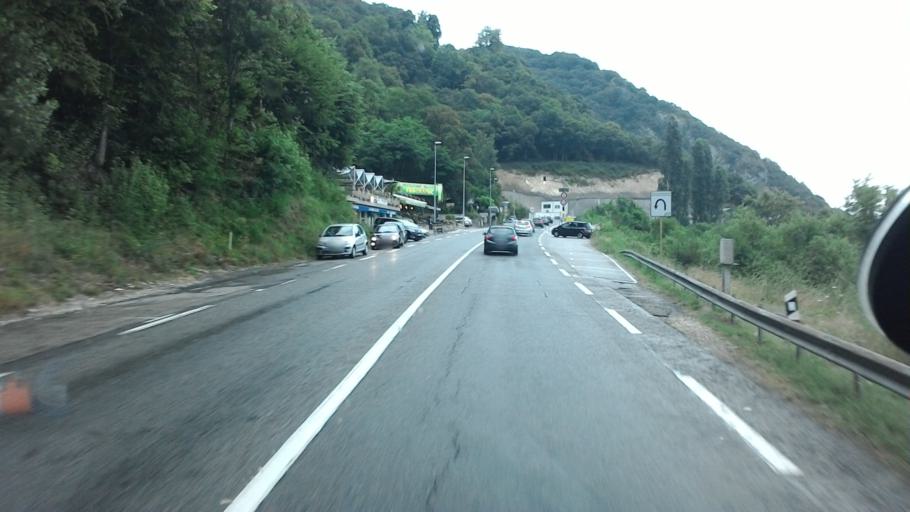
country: FR
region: Rhone-Alpes
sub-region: Departement de la Savoie
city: Le Bourget-du-Lac
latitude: 45.6834
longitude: 5.8513
